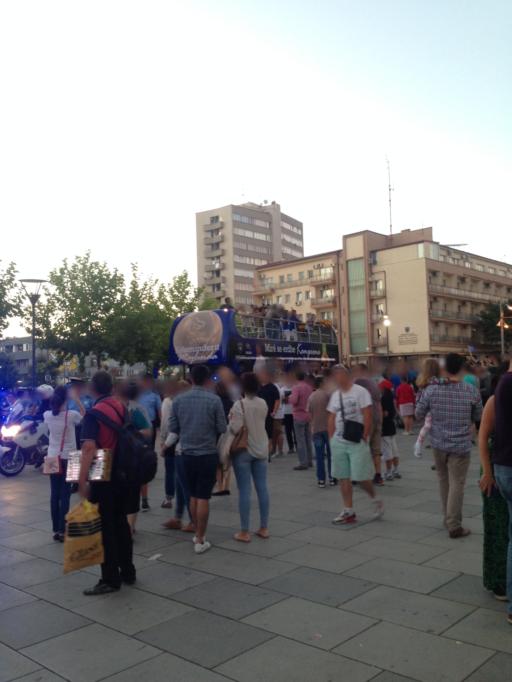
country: XK
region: Pristina
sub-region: Komuna e Prishtines
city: Pristina
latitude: 42.6600
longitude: 21.1610
